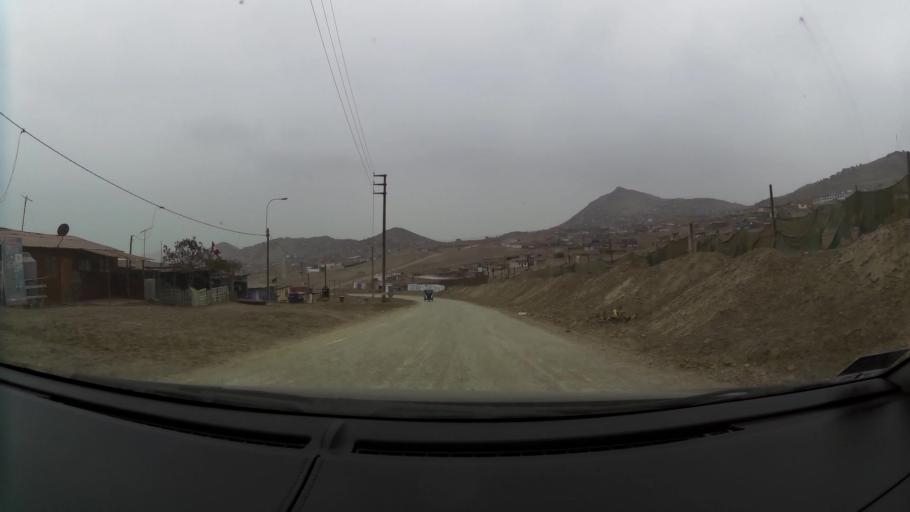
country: PE
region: Lima
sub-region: Lima
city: Santa Rosa
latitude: -11.8231
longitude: -77.1645
